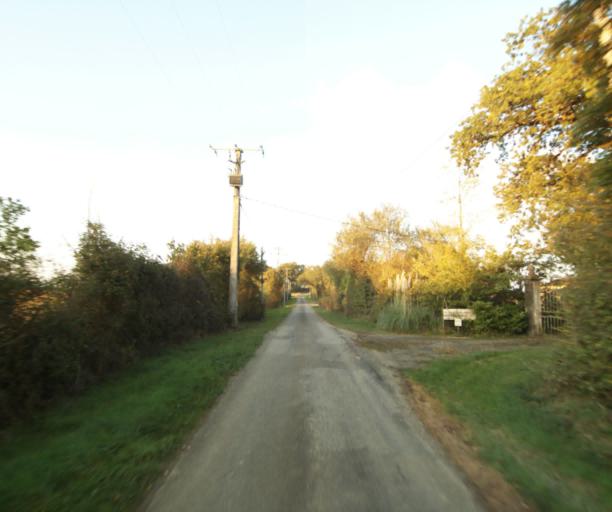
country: FR
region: Midi-Pyrenees
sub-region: Departement du Gers
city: Vic-Fezensac
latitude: 43.7770
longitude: 0.2010
